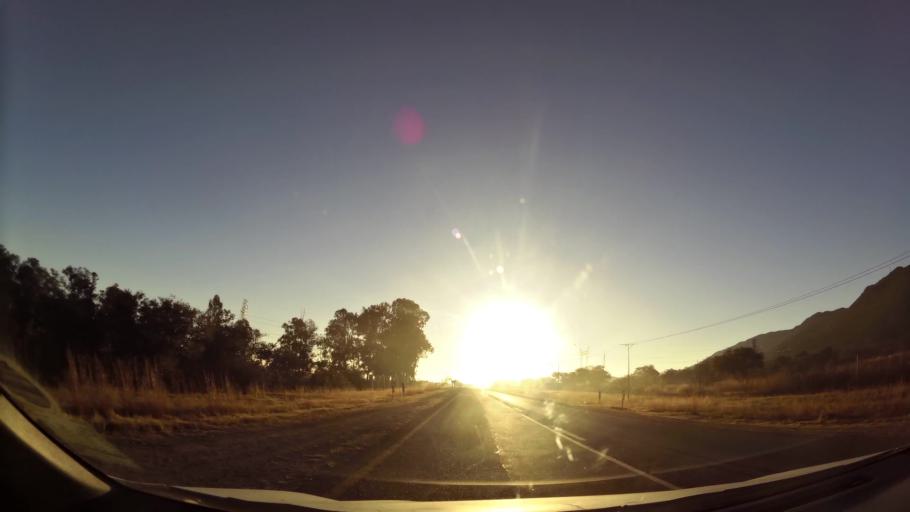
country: ZA
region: Limpopo
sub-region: Capricorn District Municipality
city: Polokwane
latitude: -24.0211
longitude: 29.3054
